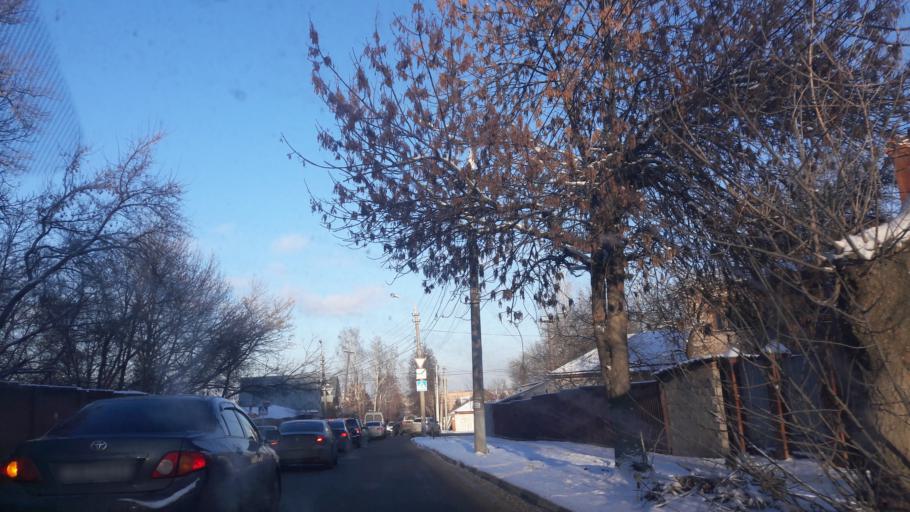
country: RU
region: Tula
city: Tula
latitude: 54.1796
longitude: 37.6163
